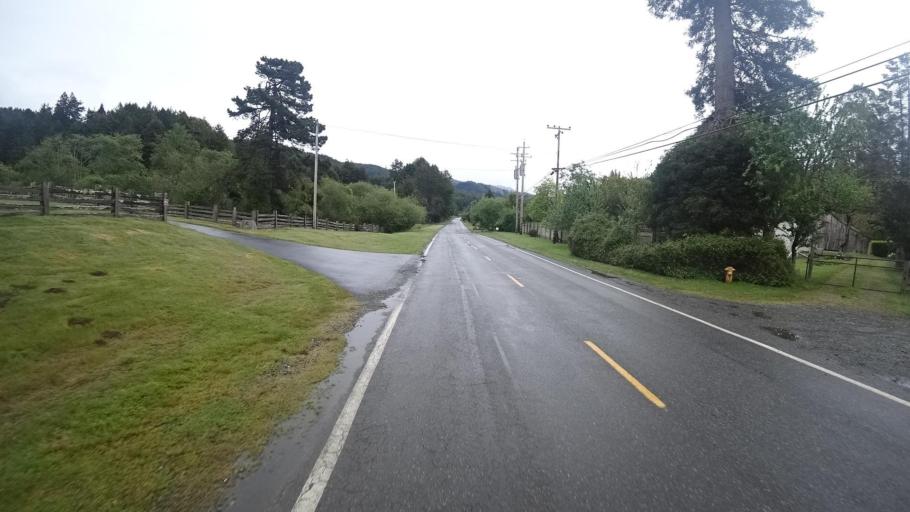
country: US
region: California
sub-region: Humboldt County
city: Bayside
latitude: 40.8355
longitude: -124.0490
